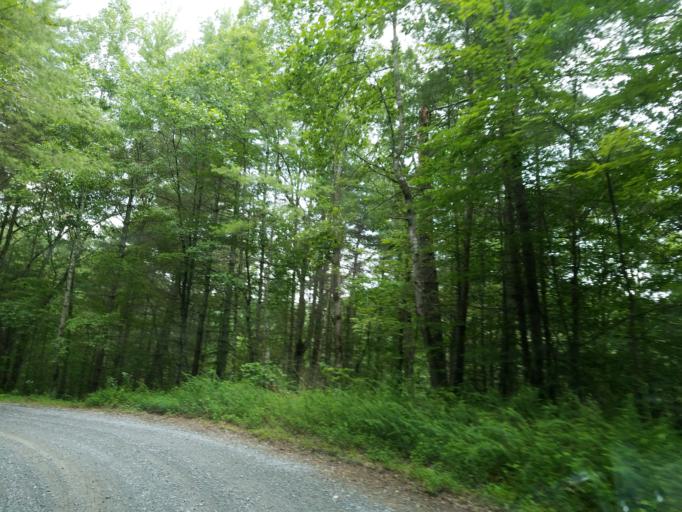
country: US
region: Georgia
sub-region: Fannin County
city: Blue Ridge
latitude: 34.8180
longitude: -84.2406
